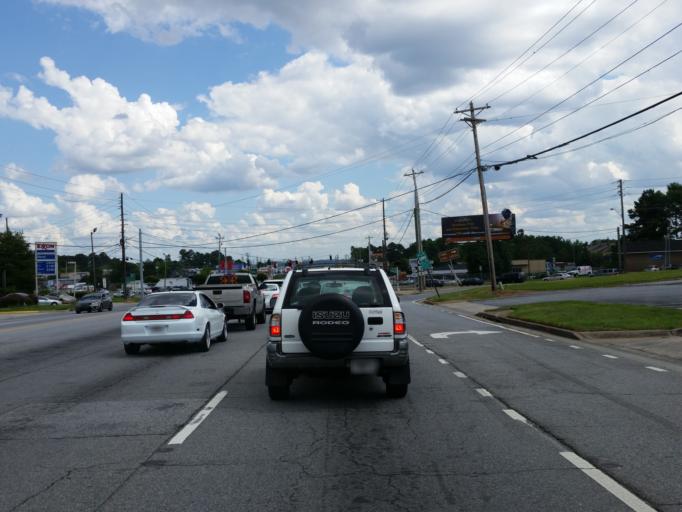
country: US
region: Georgia
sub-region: Cobb County
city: Marietta
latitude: 33.9428
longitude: -84.5164
